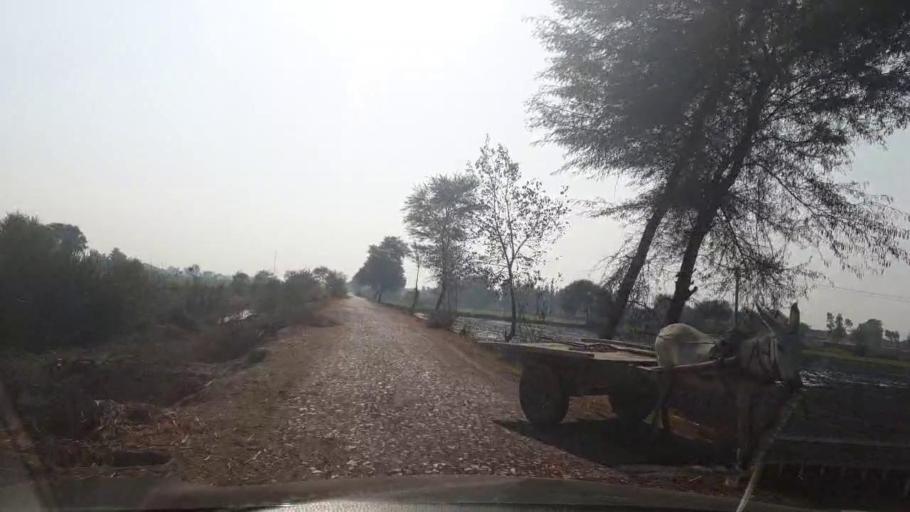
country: PK
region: Sindh
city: Khairpur
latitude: 28.1177
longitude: 69.6410
